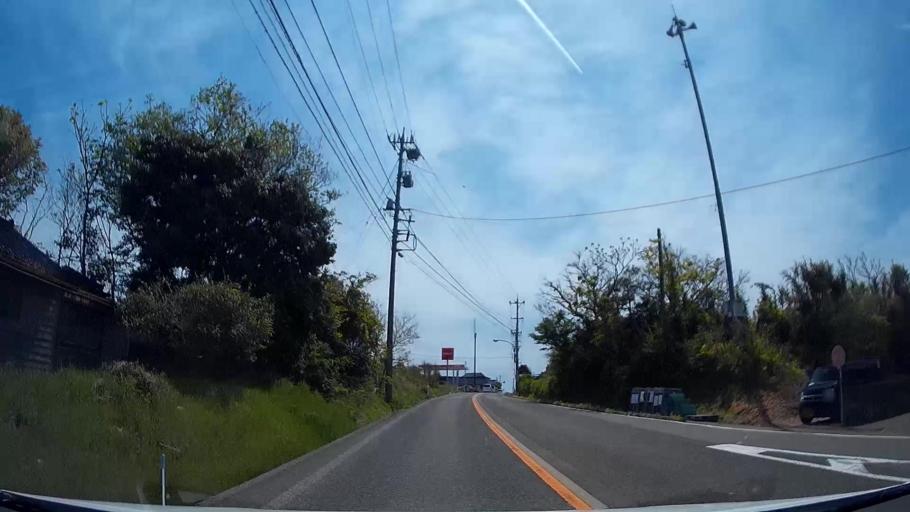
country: JP
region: Ishikawa
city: Hakui
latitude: 36.9445
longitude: 136.7633
